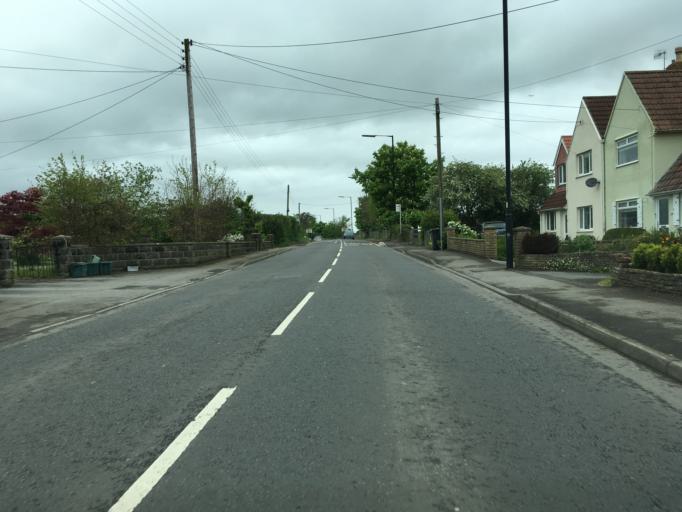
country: GB
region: England
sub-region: North Somerset
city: Banwell
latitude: 51.3299
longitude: -2.8797
